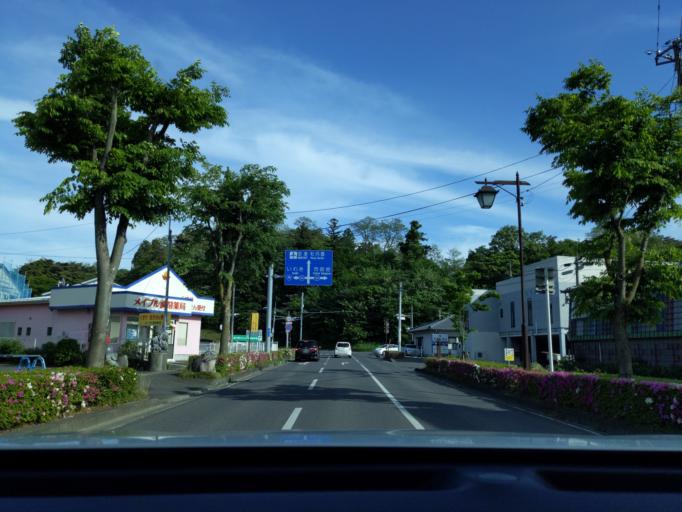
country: JP
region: Fukushima
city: Sukagawa
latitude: 37.2949
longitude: 140.3808
